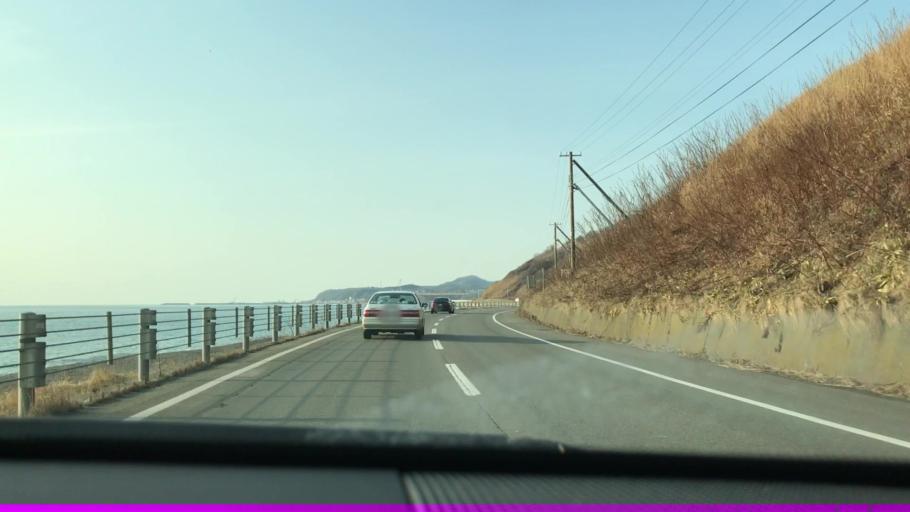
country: JP
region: Hokkaido
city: Shizunai-furukawacho
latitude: 42.2333
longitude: 142.6028
